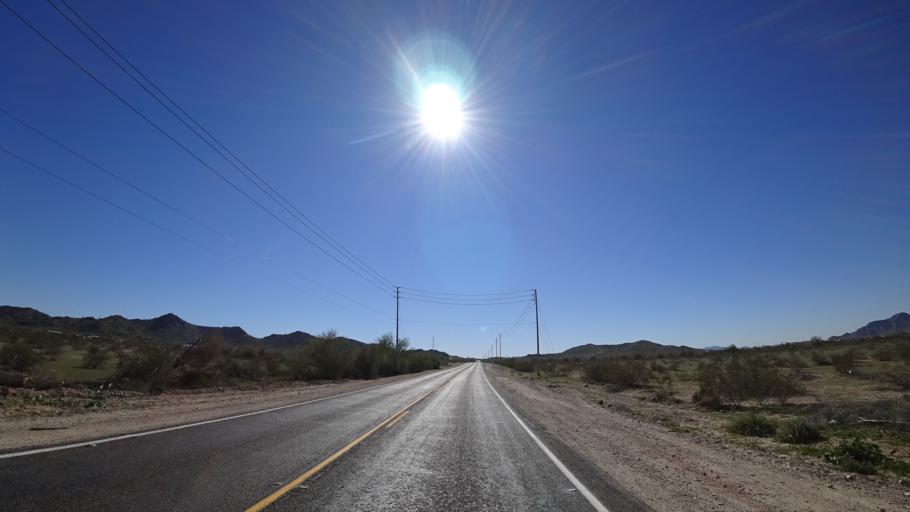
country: US
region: Arizona
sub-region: Maricopa County
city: Buckeye
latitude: 33.3265
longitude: -112.4700
